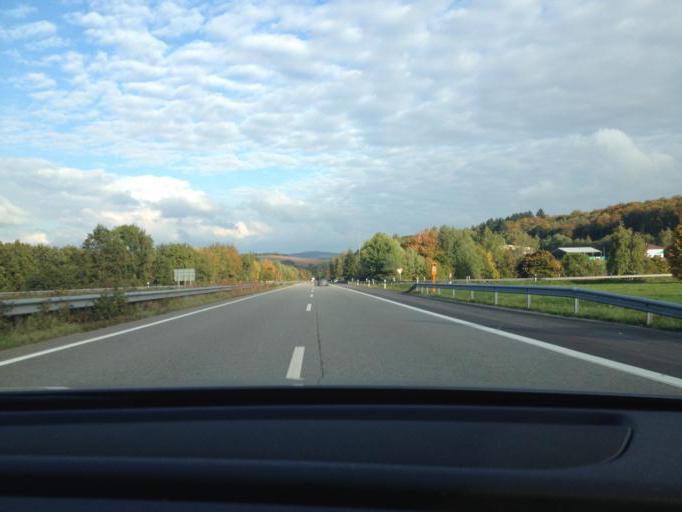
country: DE
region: Rheinland-Pfalz
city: Ehweiler
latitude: 49.5156
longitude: 7.3683
